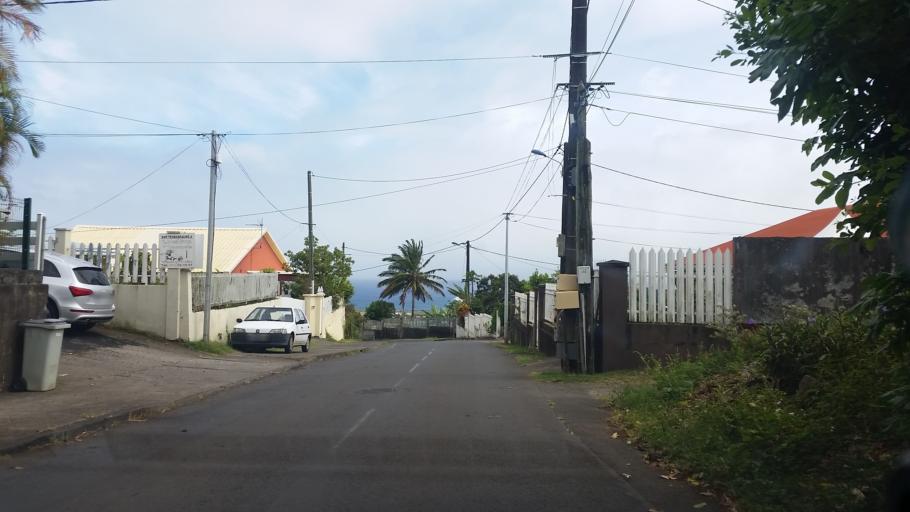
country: RE
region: Reunion
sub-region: Reunion
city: Sainte-Marie
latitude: -20.9185
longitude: 55.5315
